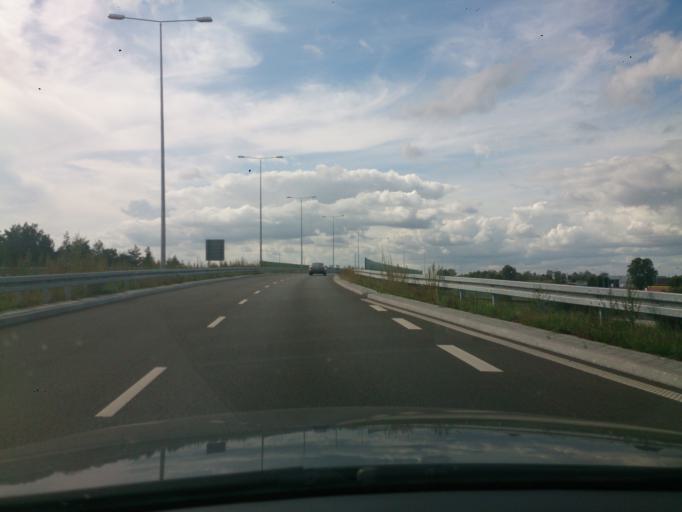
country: PL
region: Kujawsko-Pomorskie
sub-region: Grudziadz
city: Grudziadz
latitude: 53.4474
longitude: 18.7313
